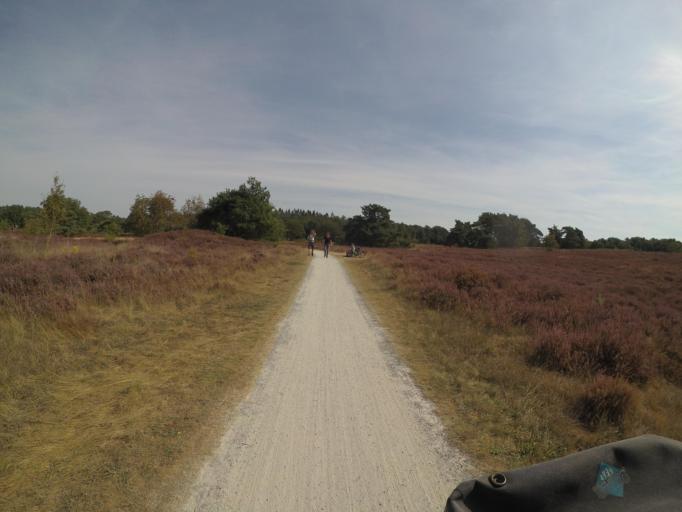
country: NL
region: Drenthe
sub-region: Gemeente Westerveld
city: Havelte
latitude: 52.7952
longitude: 6.2337
